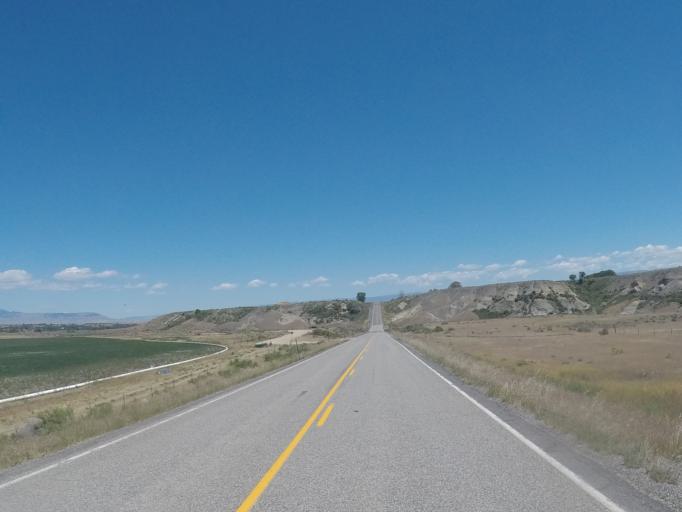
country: US
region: Wyoming
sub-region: Big Horn County
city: Lovell
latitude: 44.7745
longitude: -108.5035
